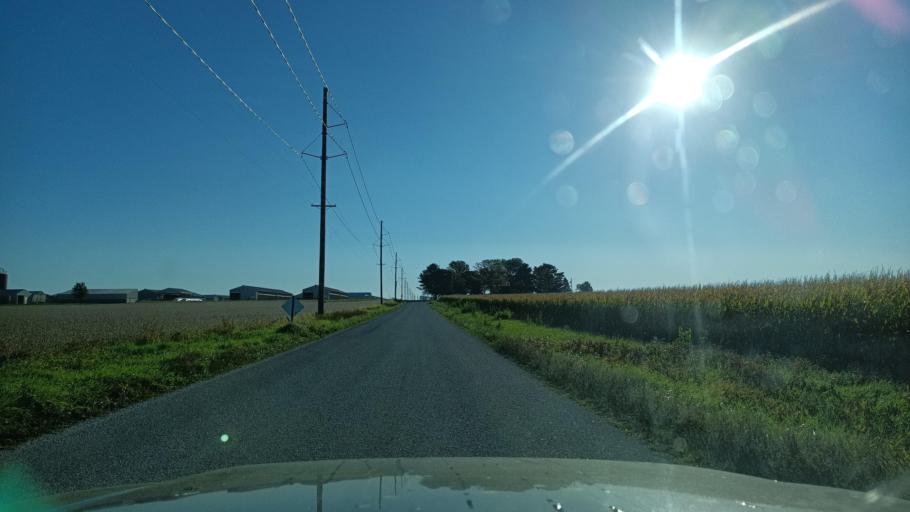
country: US
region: Illinois
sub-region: Champaign County
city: Savoy
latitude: 40.0545
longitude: -88.2126
